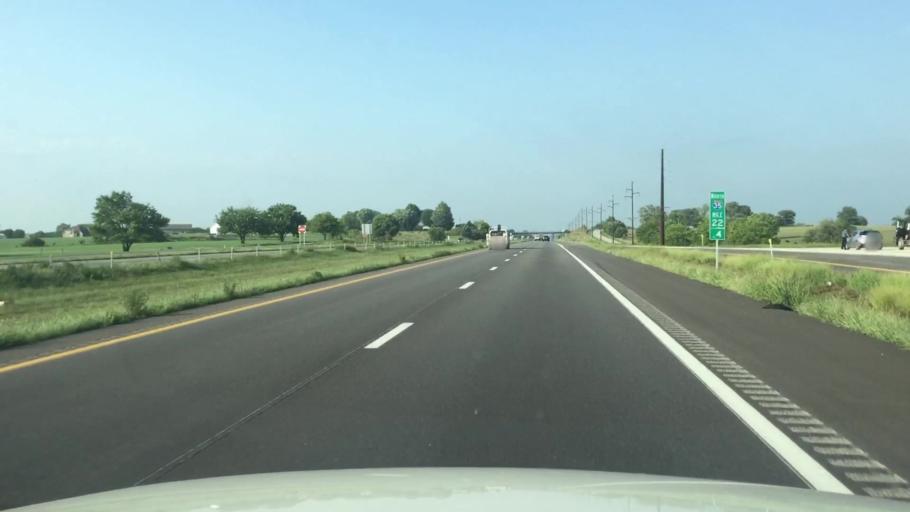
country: US
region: Missouri
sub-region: Clay County
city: Kearney
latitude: 39.3174
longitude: -94.3992
